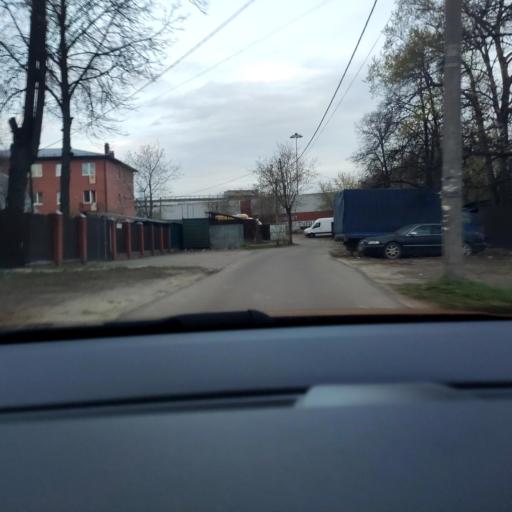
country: RU
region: Moscow
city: Yaroslavskiy
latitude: 55.8847
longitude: 37.7255
